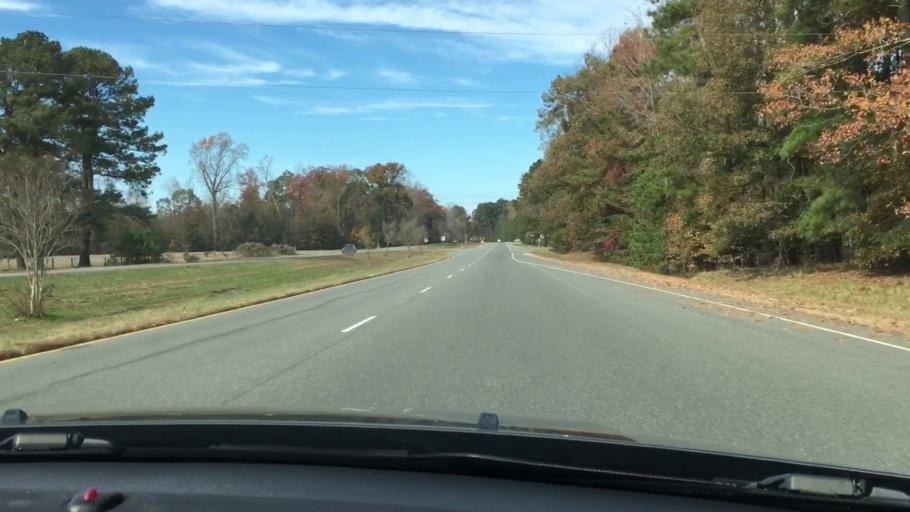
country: US
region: Virginia
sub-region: King William County
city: West Point
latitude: 37.4250
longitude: -76.8269
